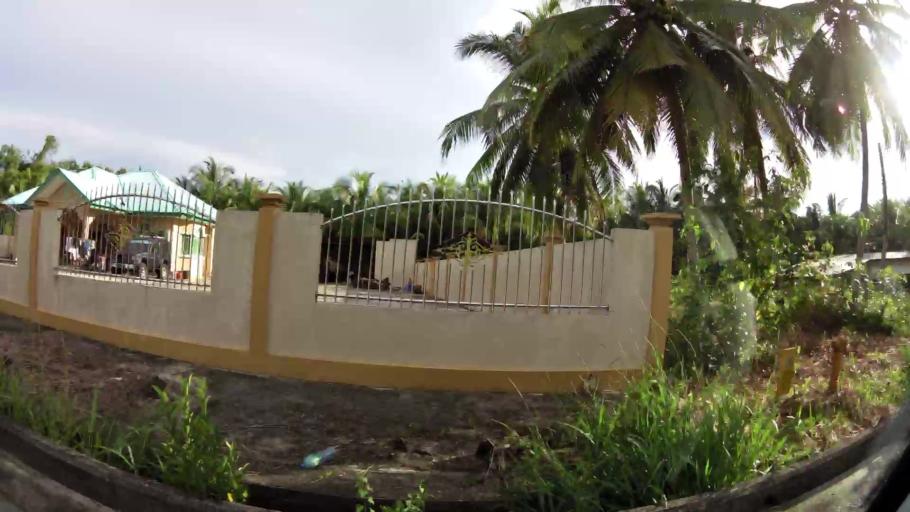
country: BN
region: Brunei and Muara
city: Bandar Seri Begawan
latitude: 4.9518
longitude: 115.0237
